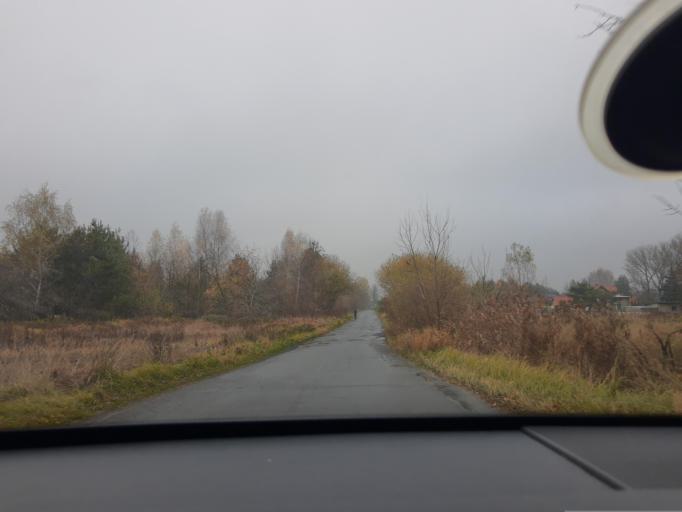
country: PL
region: Lodz Voivodeship
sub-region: Powiat pabianicki
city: Konstantynow Lodzki
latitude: 51.7472
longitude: 19.3716
